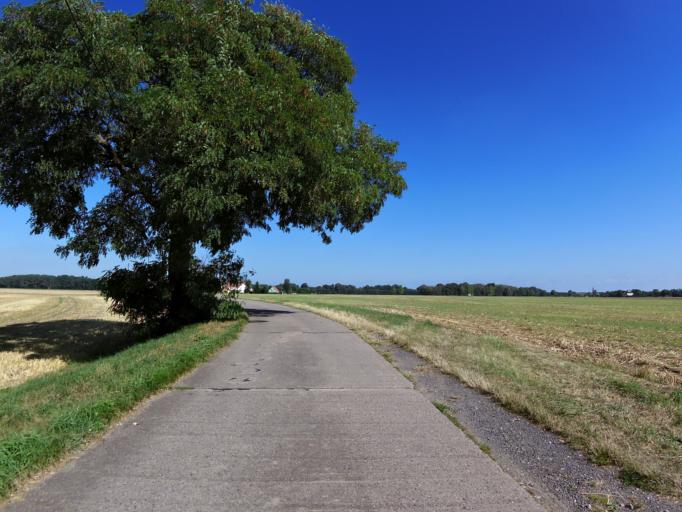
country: DE
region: Saxony
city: Strehla
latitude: 51.3572
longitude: 13.2415
